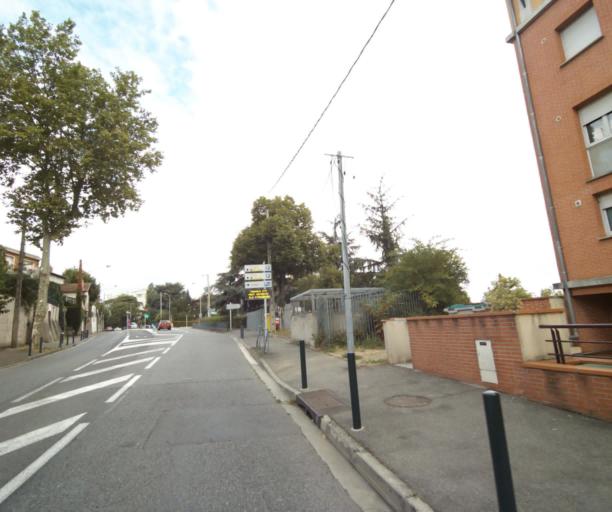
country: FR
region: Midi-Pyrenees
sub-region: Departement de la Haute-Garonne
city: Balma
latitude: 43.6004
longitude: 1.4771
